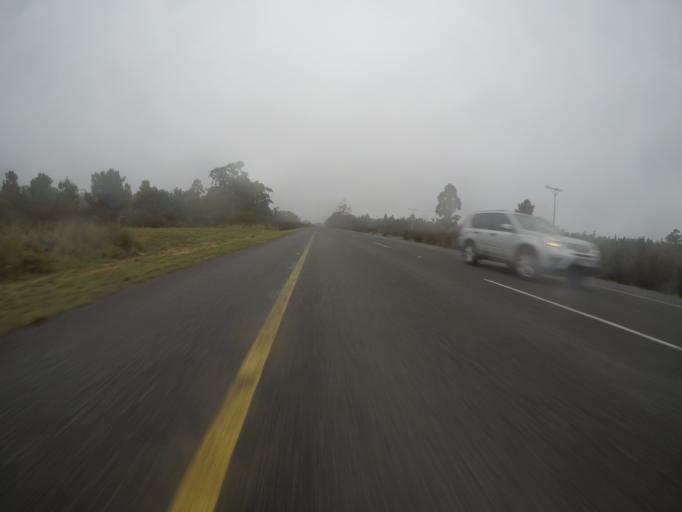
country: ZA
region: Western Cape
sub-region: Eden District Municipality
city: Riversdale
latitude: -34.1864
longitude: 21.4370
